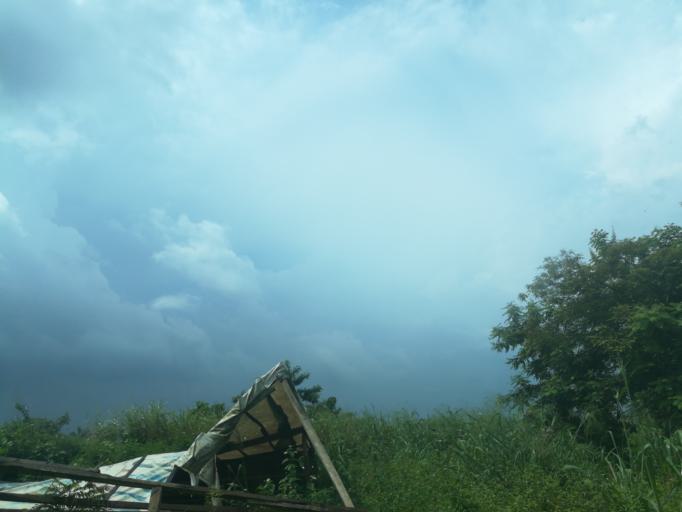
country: NG
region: Lagos
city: Ikorodu
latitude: 6.6471
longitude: 3.5664
